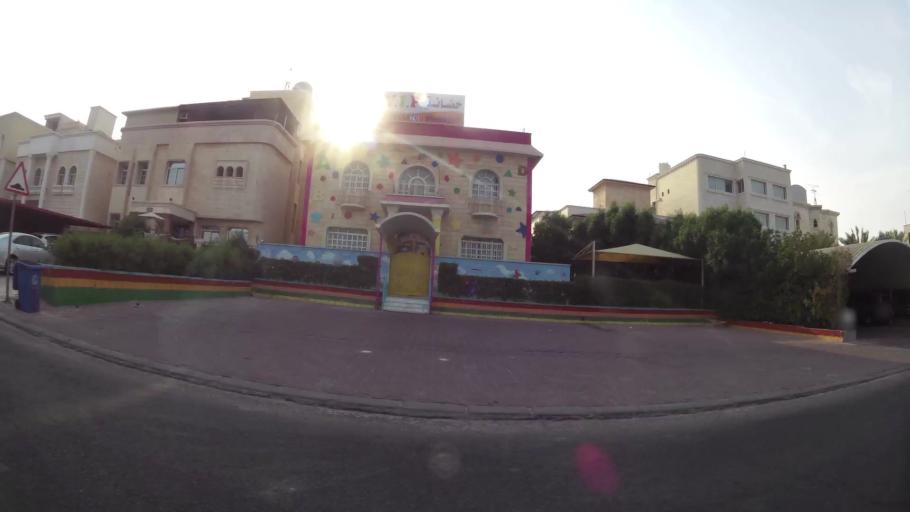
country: KW
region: Mubarak al Kabir
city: Mubarak al Kabir
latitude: 29.1864
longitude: 48.0718
